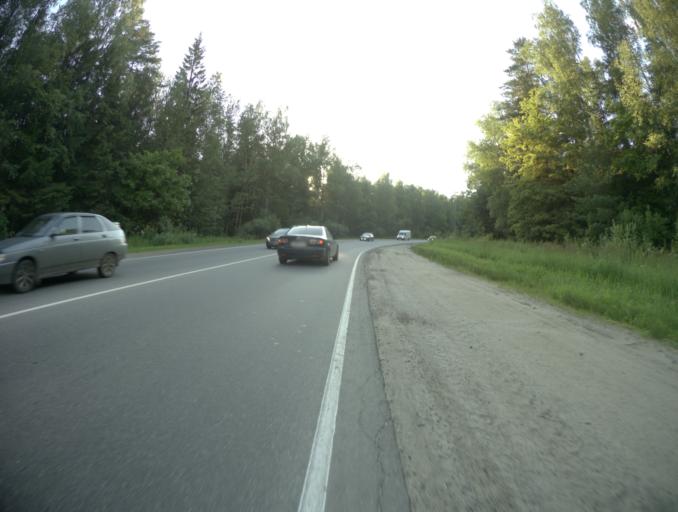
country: RU
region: Vladimir
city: Kommunar
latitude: 56.0209
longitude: 40.5767
